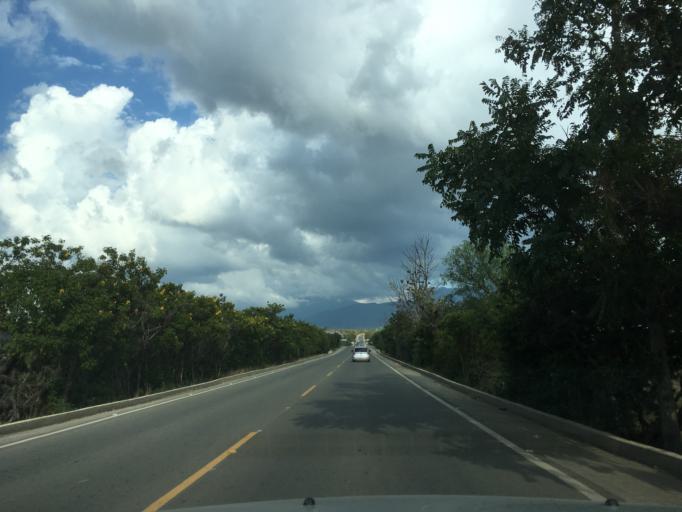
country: CO
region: Boyaca
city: Sutamarchan
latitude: 5.6235
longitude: -73.5958
